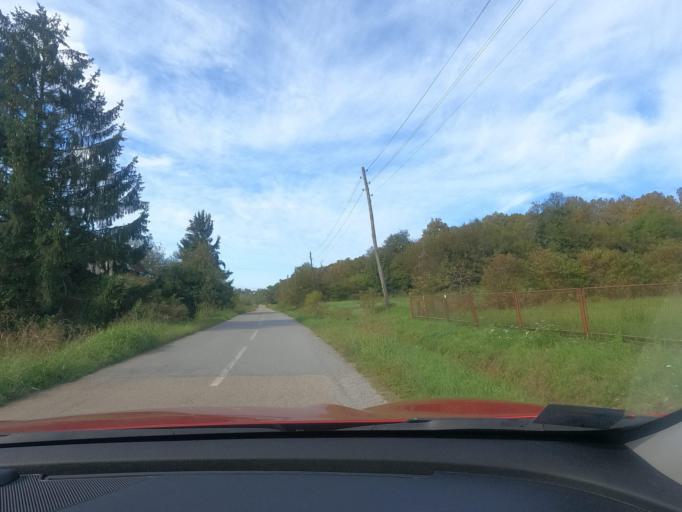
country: HR
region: Sisacko-Moslavacka
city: Glina
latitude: 45.3079
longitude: 16.1828
